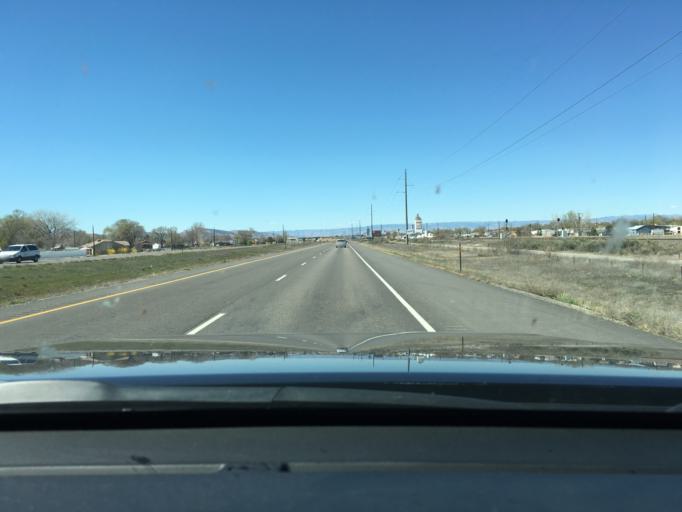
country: US
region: Colorado
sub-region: Mesa County
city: Fruita
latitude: 39.1495
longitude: -108.7239
